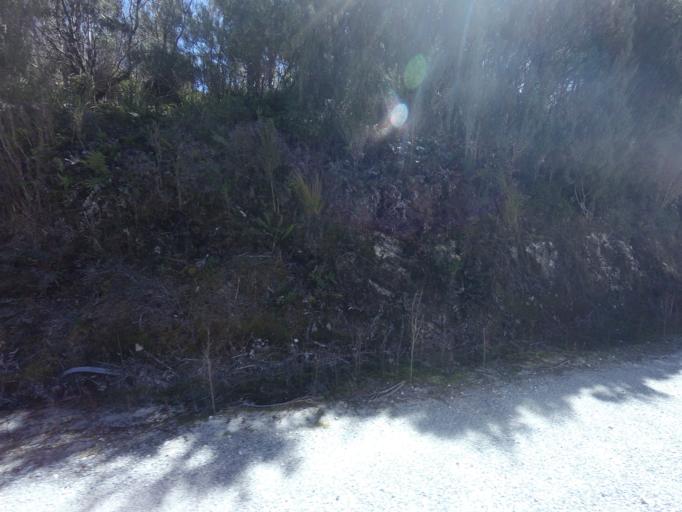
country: AU
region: Tasmania
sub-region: West Coast
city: Queenstown
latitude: -42.7653
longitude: 145.9861
